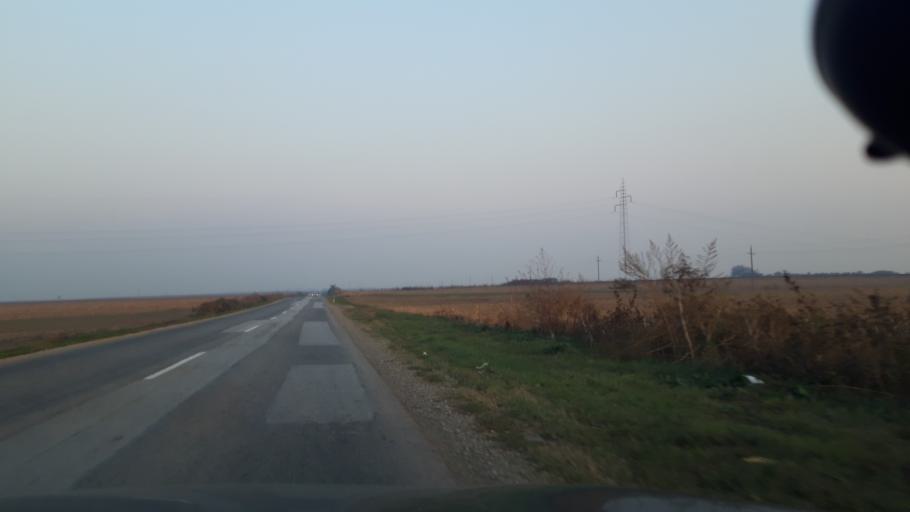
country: RS
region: Autonomna Pokrajina Vojvodina
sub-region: Sremski Okrug
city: Ruma
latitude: 45.0087
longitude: 19.8933
